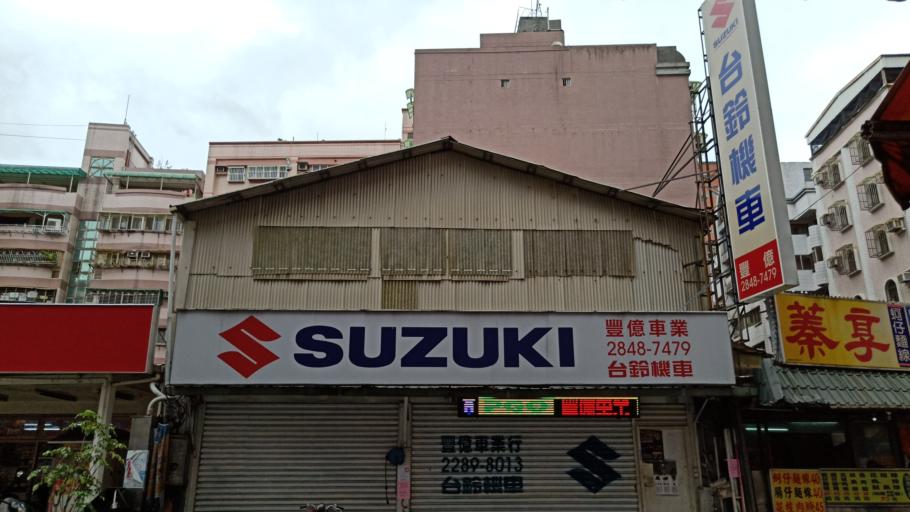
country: TW
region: Taipei
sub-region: Taipei
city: Banqiao
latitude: 25.0884
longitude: 121.4573
